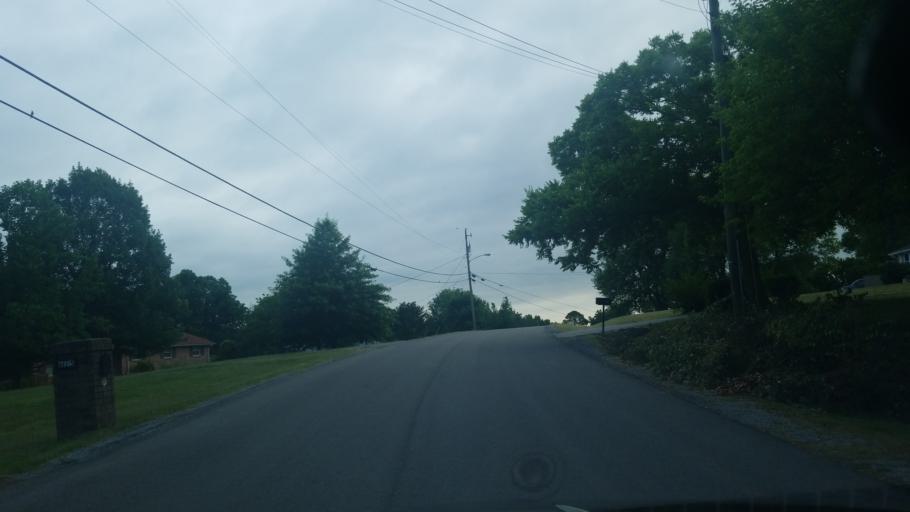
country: US
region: Tennessee
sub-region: Davidson County
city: Nashville
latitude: 36.2307
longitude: -86.7415
